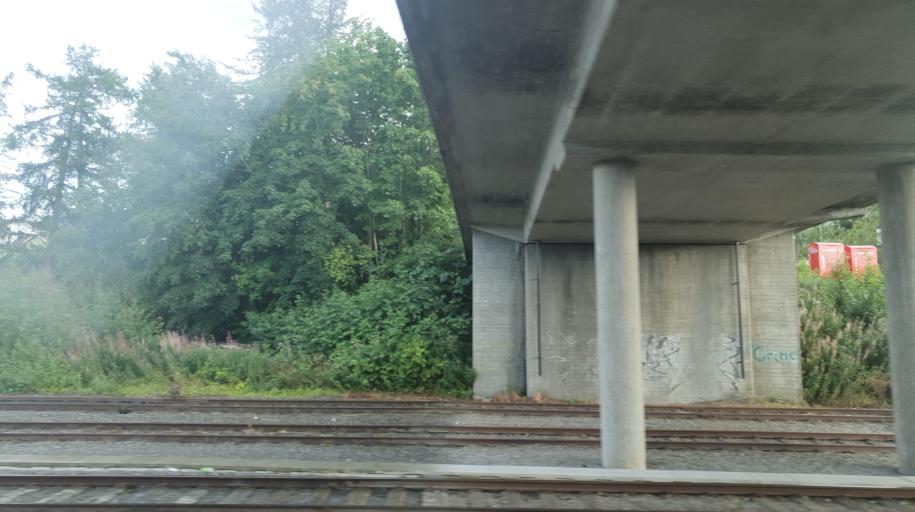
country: NO
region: Nord-Trondelag
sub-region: Levanger
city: Levanger
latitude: 63.7436
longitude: 11.2983
